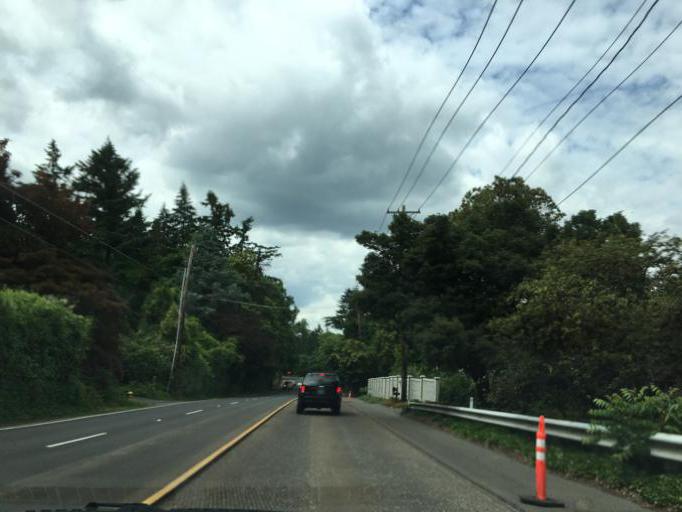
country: US
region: Oregon
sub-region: Clackamas County
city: Milwaukie
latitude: 45.4510
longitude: -122.6592
